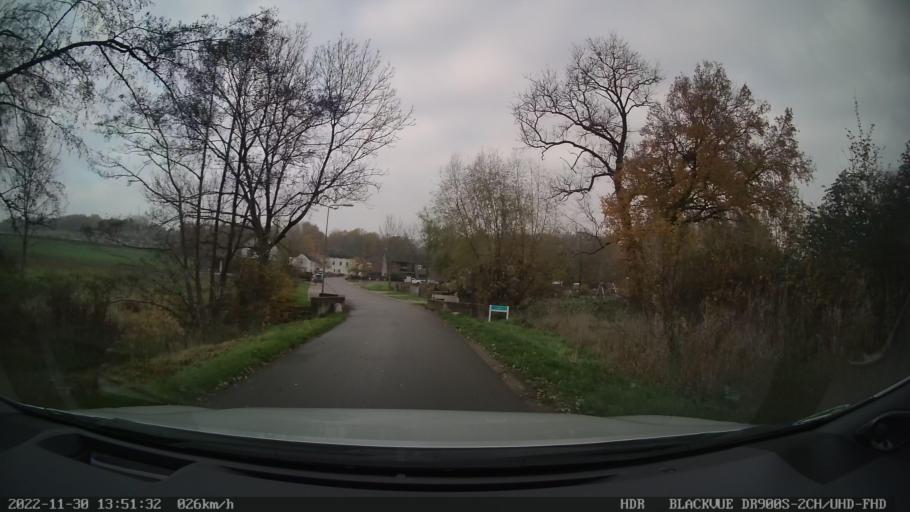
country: NL
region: Limburg
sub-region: Valkenburg aan de Geul
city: Schin op Geul
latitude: 50.8013
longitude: 5.8700
